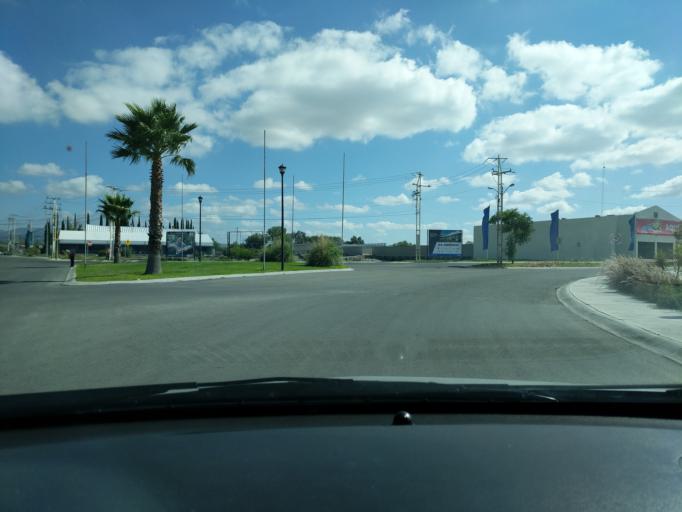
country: MX
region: Queretaro
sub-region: Queretaro
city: Patria Nueva
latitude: 20.6287
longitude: -100.4979
